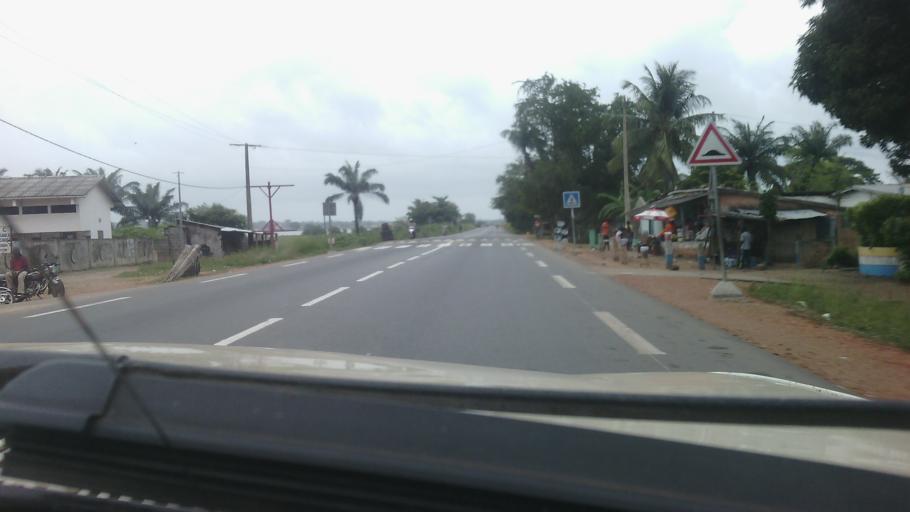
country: BJ
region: Mono
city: Come
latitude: 6.3986
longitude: 1.9244
